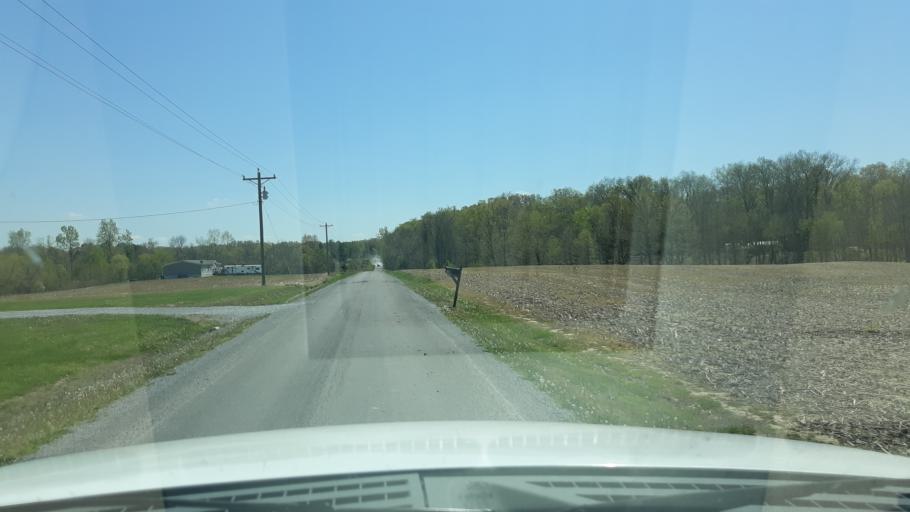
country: US
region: Illinois
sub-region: Saline County
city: Harrisburg
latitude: 37.8765
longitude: -88.6421
